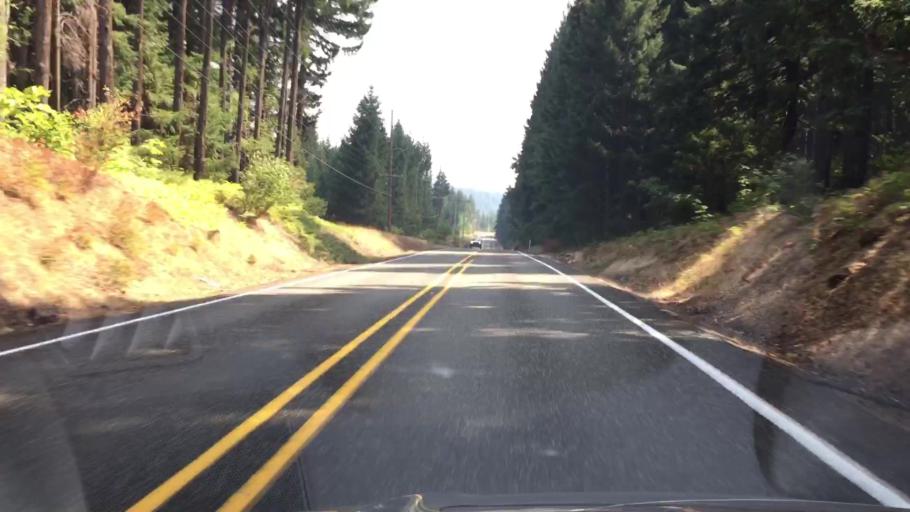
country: US
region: Washington
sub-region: Klickitat County
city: White Salmon
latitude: 45.8750
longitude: -121.5184
